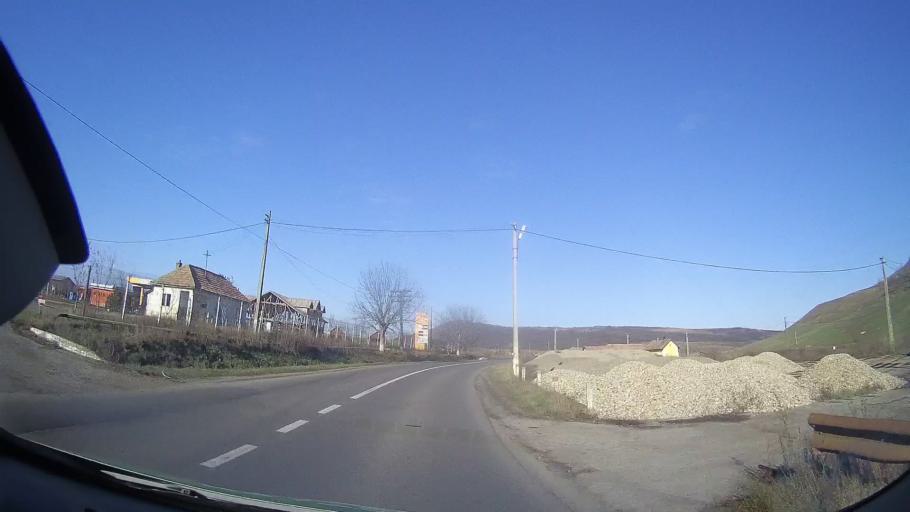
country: RO
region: Mures
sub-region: Comuna Mihesu de Campie
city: Mihesu de Campie
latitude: 46.6605
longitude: 24.1753
